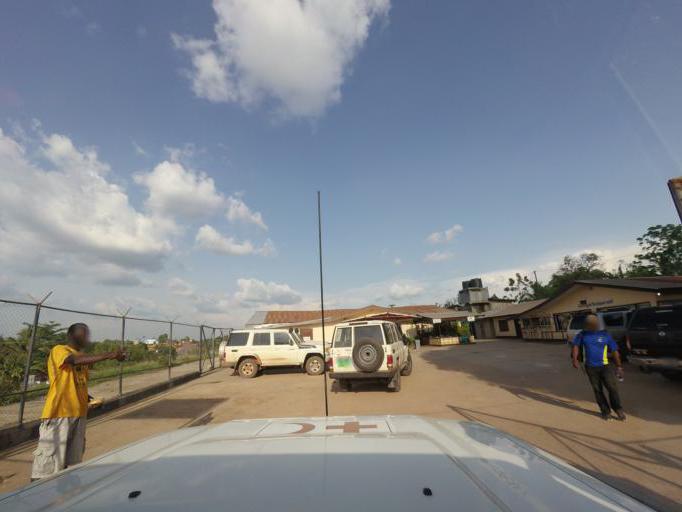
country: LR
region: Bong
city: Gbarnga
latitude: 6.9923
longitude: -9.4560
